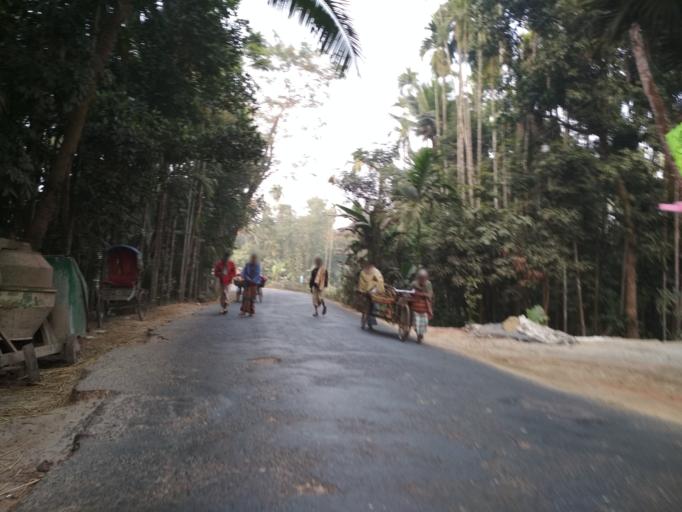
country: BD
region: Chittagong
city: Lakshmipur
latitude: 22.9173
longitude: 90.8374
